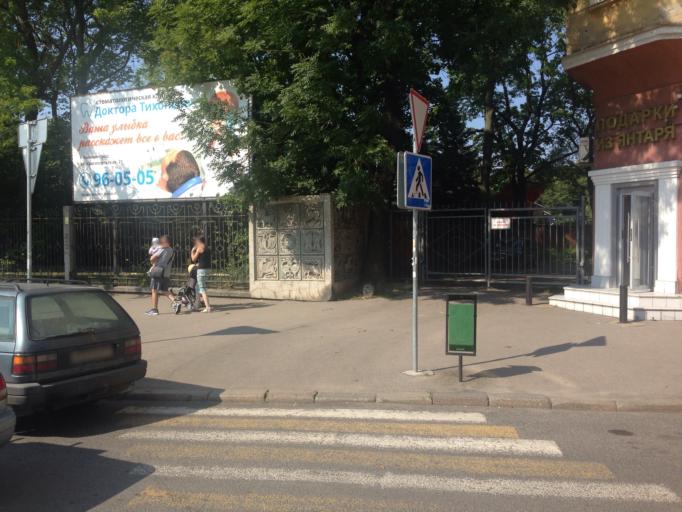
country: RU
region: Kaliningrad
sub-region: Gorod Kaliningrad
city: Kaliningrad
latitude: 54.7201
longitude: 20.4892
